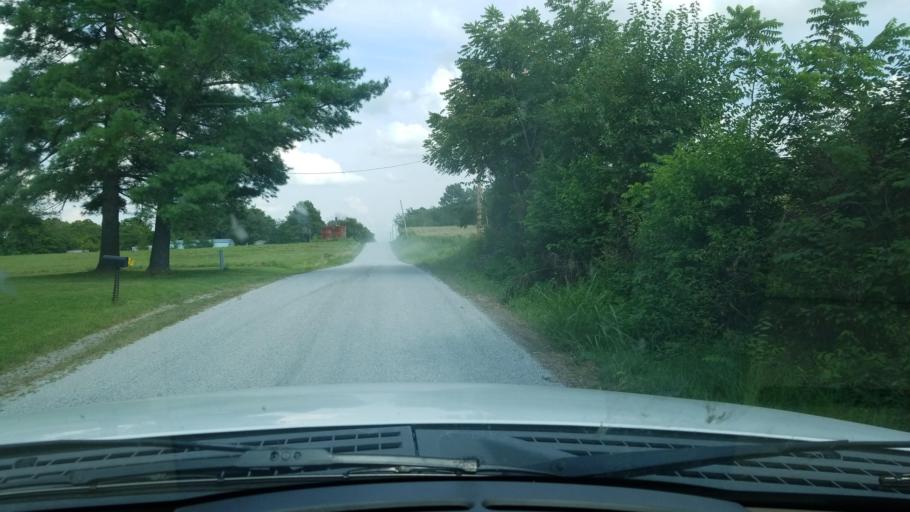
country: US
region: Illinois
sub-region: Saline County
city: Eldorado
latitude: 37.8345
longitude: -88.4366
